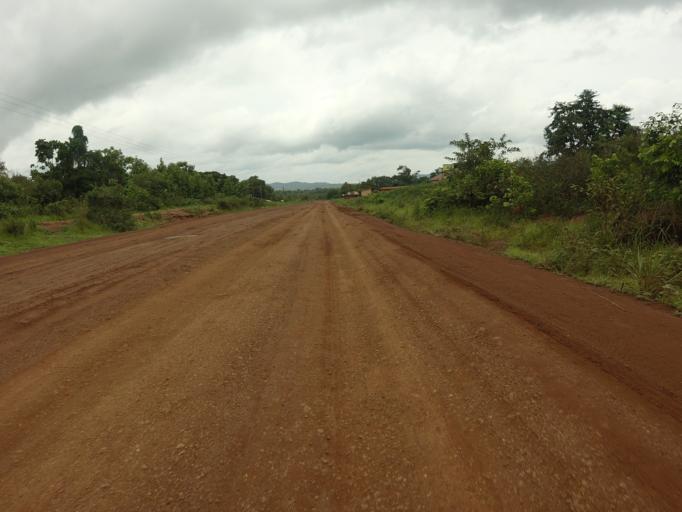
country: GH
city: Kpandae
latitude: 8.3009
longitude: 0.4862
